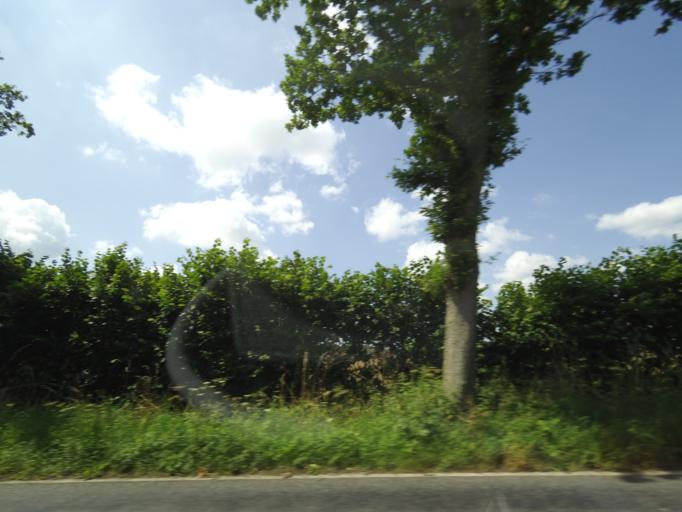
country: DK
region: South Denmark
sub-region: Assens Kommune
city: Arup
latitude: 55.3956
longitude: 10.0460
